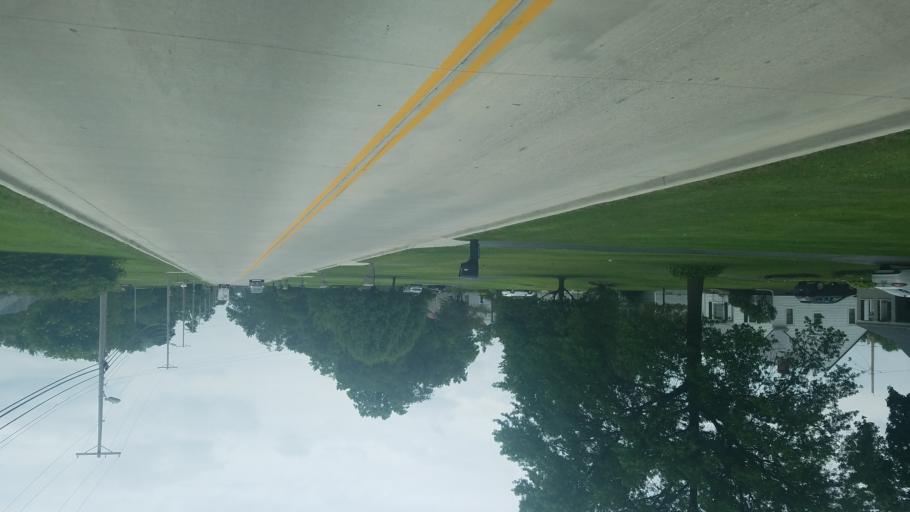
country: US
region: Ohio
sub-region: Crawford County
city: Galion
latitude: 40.7245
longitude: -82.8066
